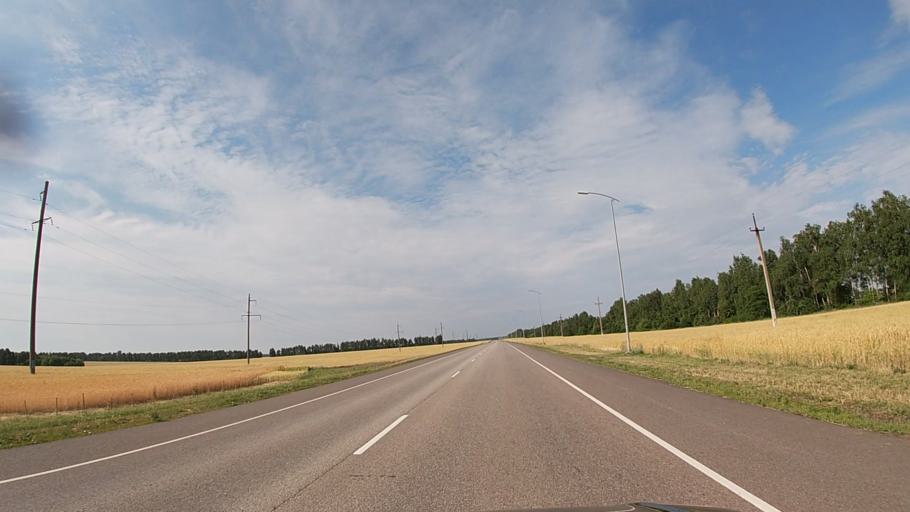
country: RU
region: Belgorod
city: Proletarskiy
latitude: 50.8274
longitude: 35.7615
